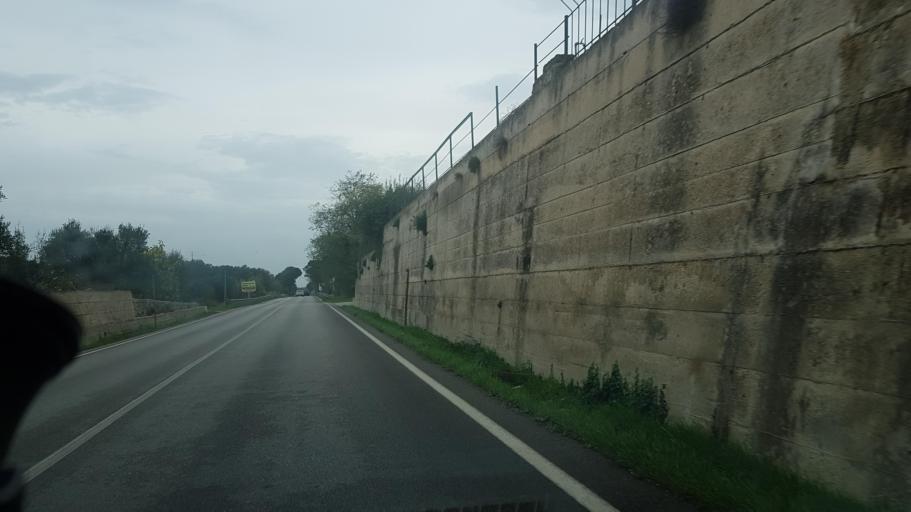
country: IT
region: Apulia
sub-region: Provincia di Brindisi
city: Ostuni
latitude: 40.7179
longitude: 17.6144
